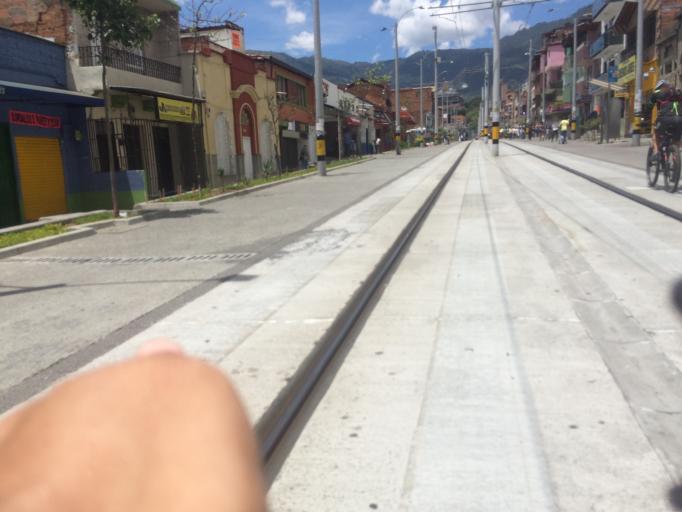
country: CO
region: Antioquia
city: Medellin
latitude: 6.2424
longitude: -75.5558
